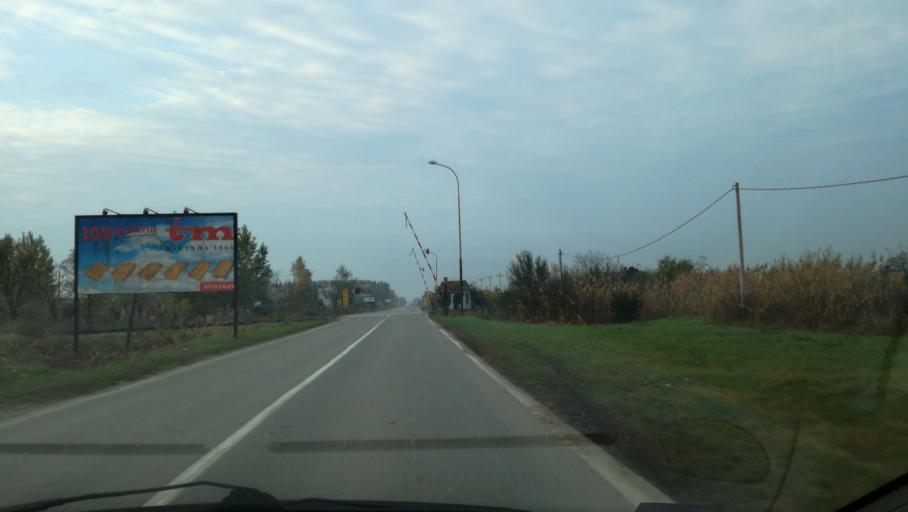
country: RS
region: Autonomna Pokrajina Vojvodina
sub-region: Severnobanatski Okrug
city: Kikinda
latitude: 45.7953
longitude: 20.4382
